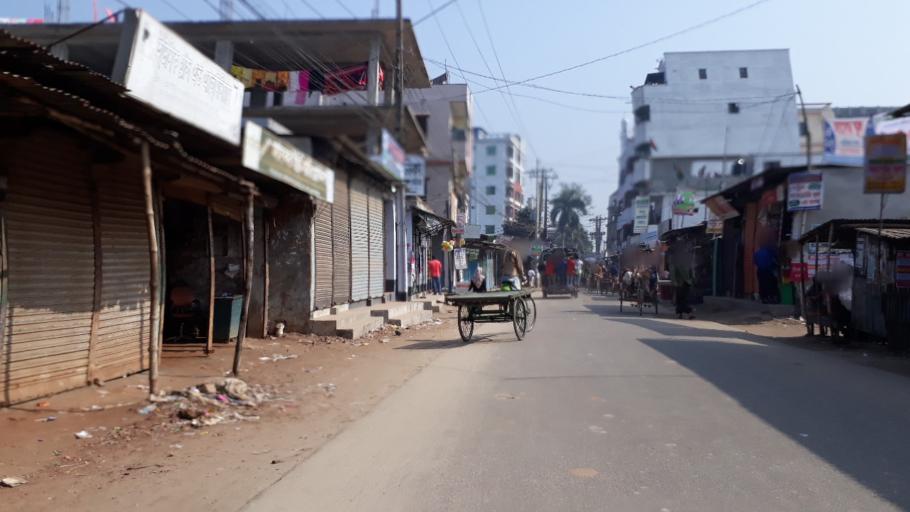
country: BD
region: Dhaka
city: Tungi
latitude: 23.8482
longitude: 90.2641
